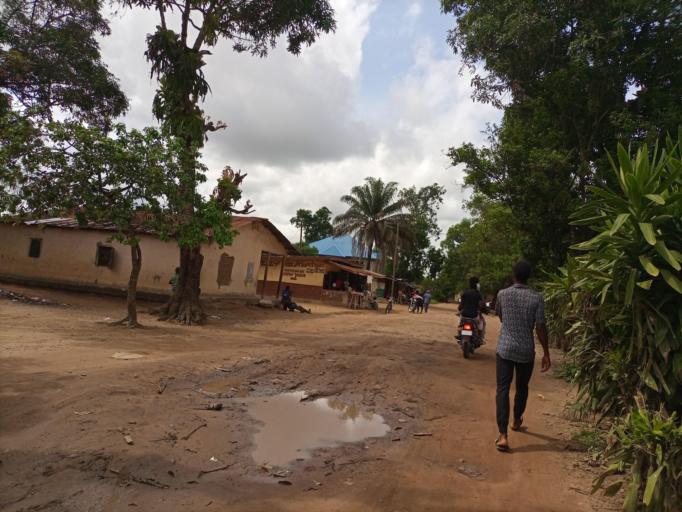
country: SL
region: Southern Province
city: Bo
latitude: 7.9634
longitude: -11.7602
